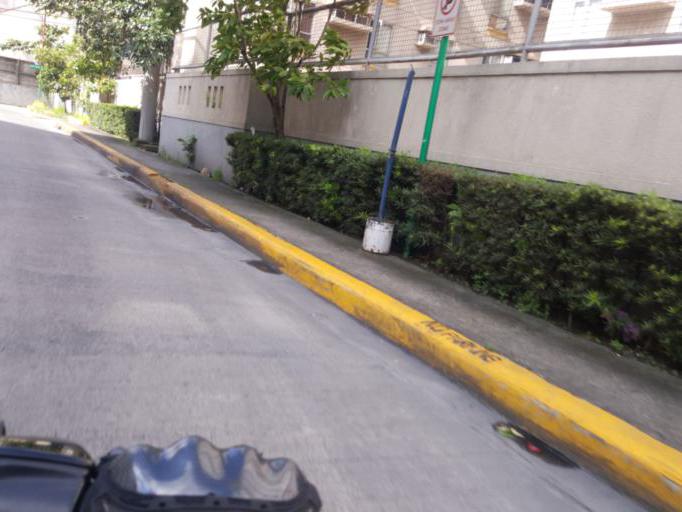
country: PH
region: Metro Manila
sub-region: City of Manila
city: Manila
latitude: 14.6187
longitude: 120.9869
